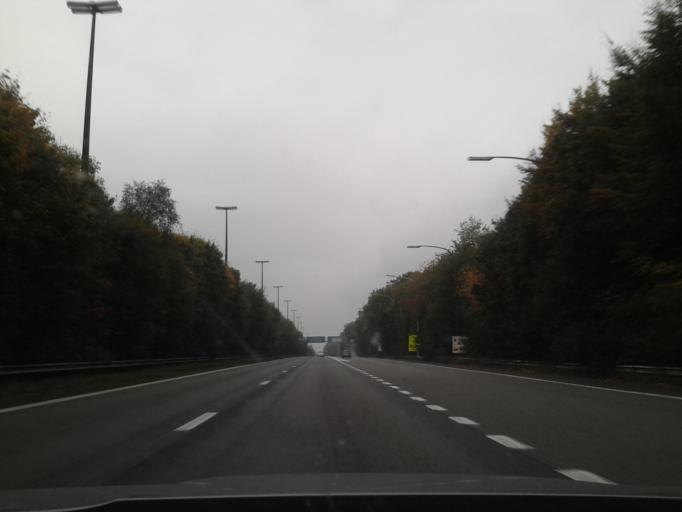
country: BE
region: Wallonia
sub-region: Province du Hainaut
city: La Louviere
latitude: 50.5247
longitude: 4.1999
